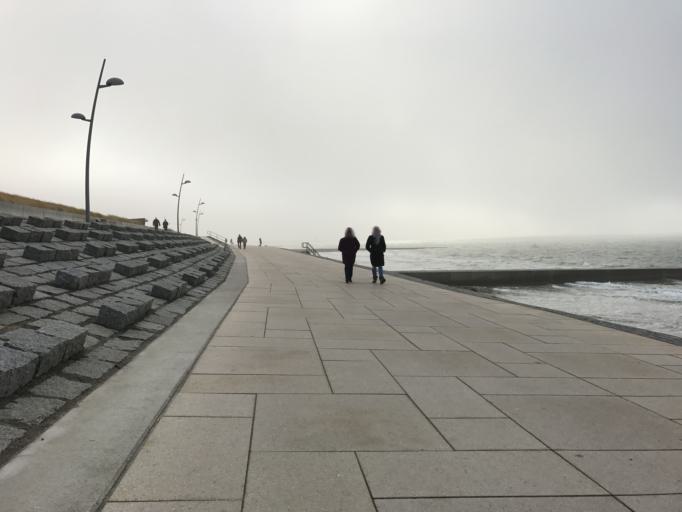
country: DE
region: Lower Saxony
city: Borkum
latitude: 53.5845
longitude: 6.6574
